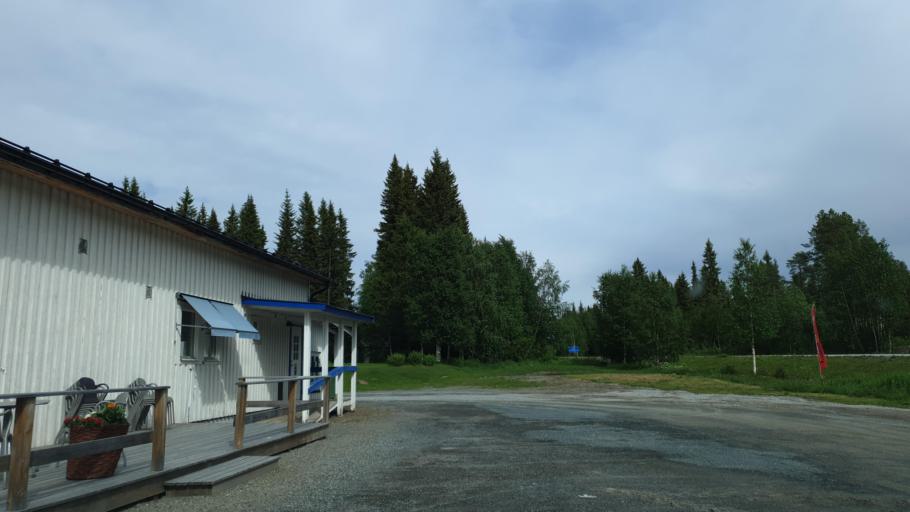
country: SE
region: Vaesterbotten
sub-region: Storumans Kommun
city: Fristad
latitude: 65.4306
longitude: 16.2485
